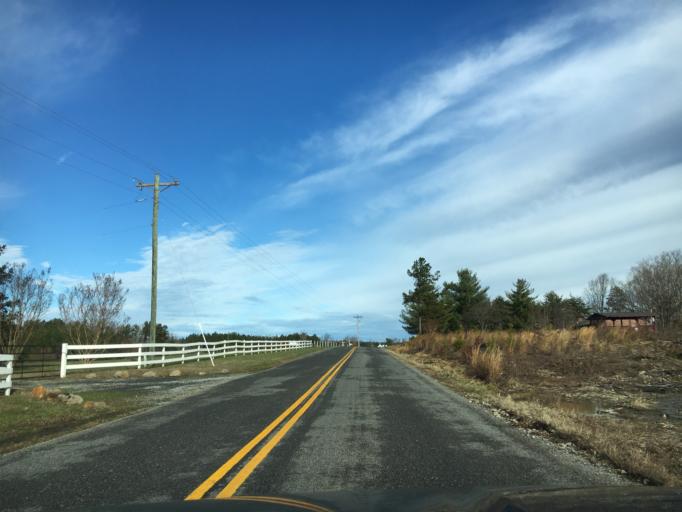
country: US
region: Virginia
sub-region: Nottoway County
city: Crewe
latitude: 37.2848
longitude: -78.2035
